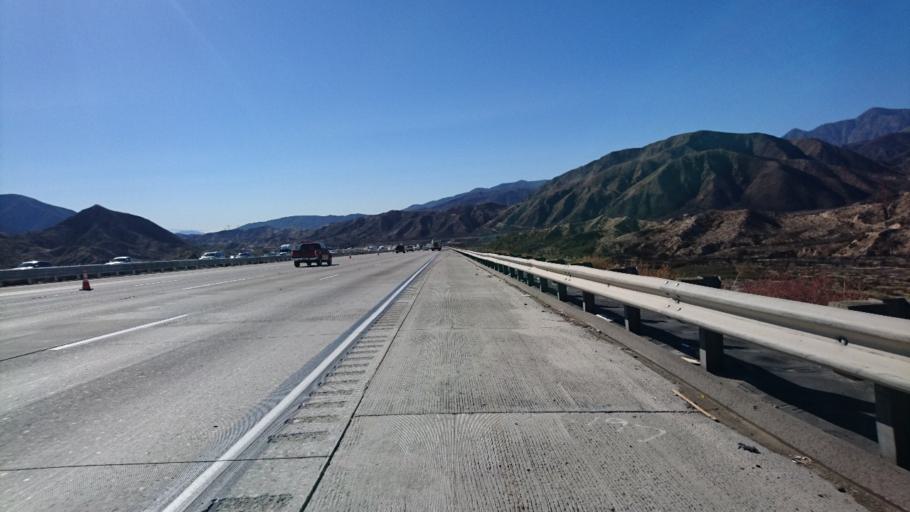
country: US
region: California
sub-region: San Bernardino County
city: Oak Hills
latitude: 34.3283
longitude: -117.4826
